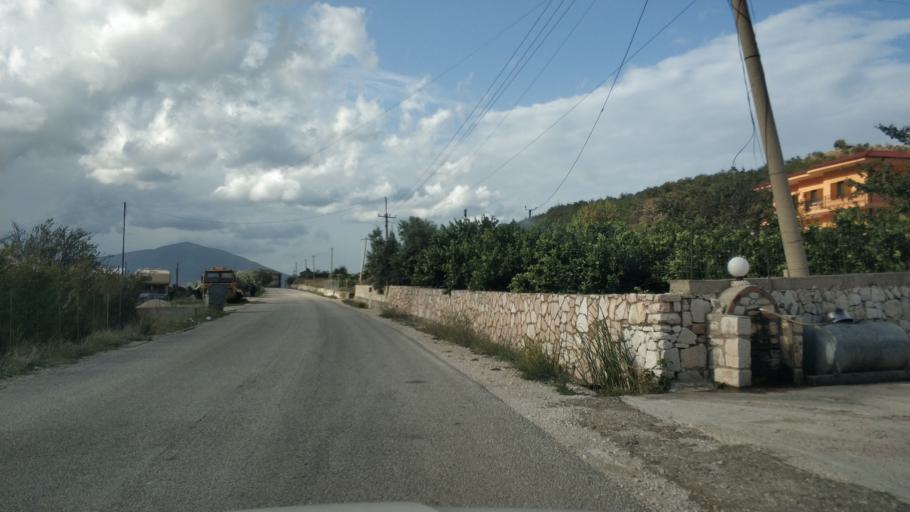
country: AL
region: Vlore
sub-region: Rrethi i Vlores
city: Orikum
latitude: 40.2967
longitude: 19.4894
